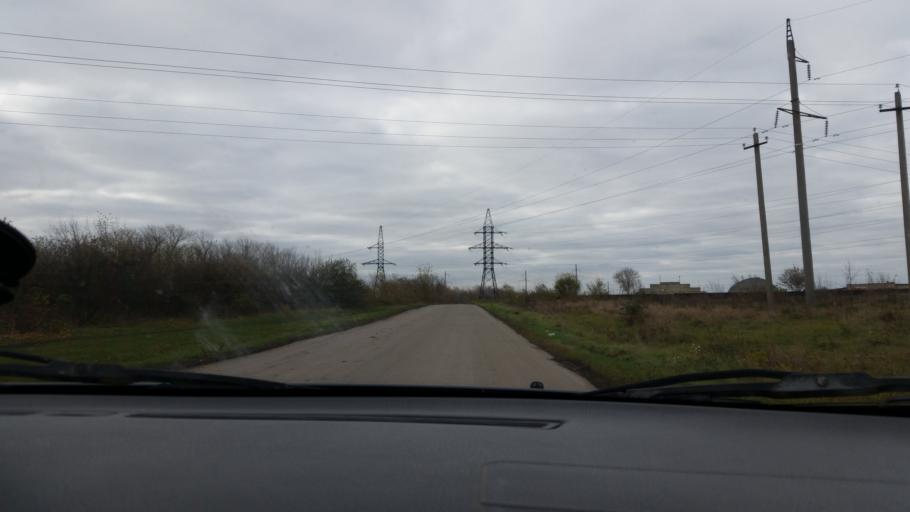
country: RU
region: Lipetsk
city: Gryazi
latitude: 52.4667
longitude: 39.9395
